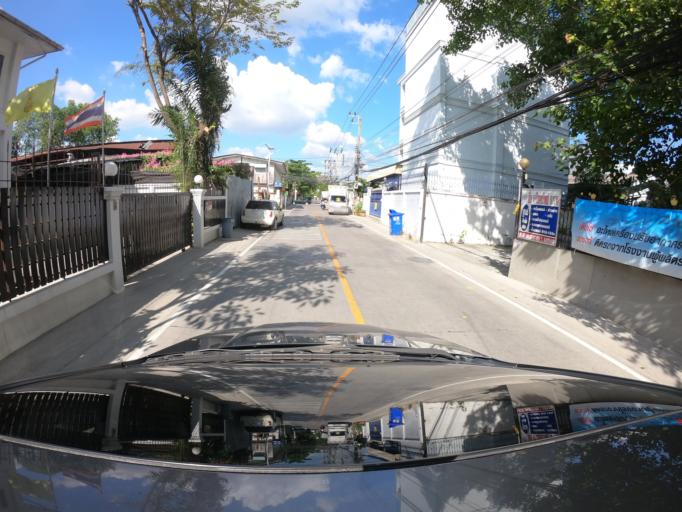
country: TH
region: Bangkok
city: Bang Na
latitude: 13.6487
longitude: 100.6247
